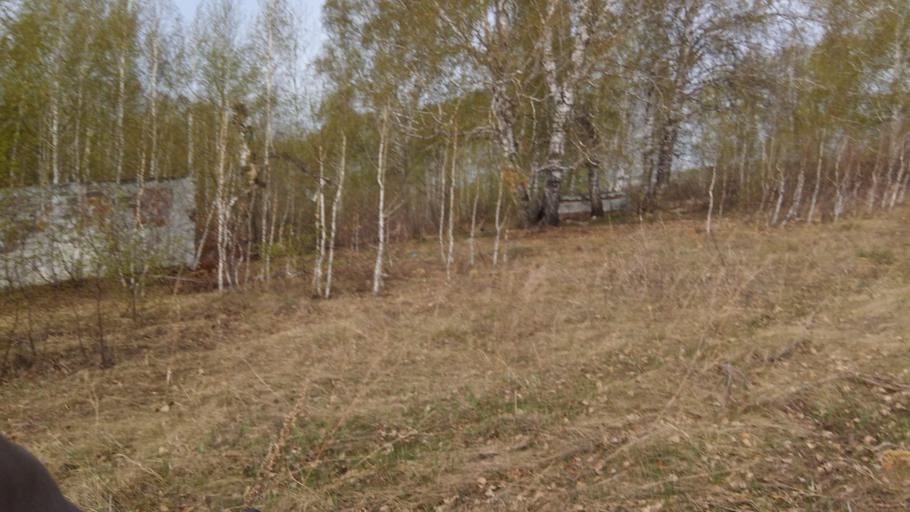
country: RU
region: Chelyabinsk
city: Timiryazevskiy
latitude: 55.0259
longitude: 60.8587
